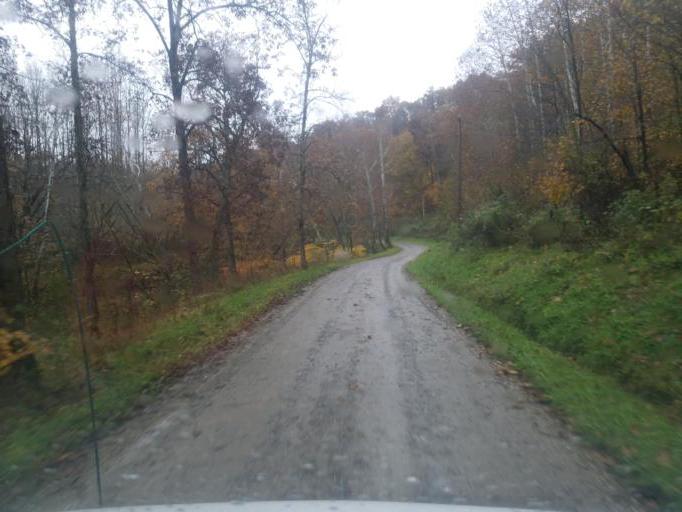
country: US
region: Ohio
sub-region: Washington County
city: Beverly
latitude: 39.4729
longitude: -81.7449
